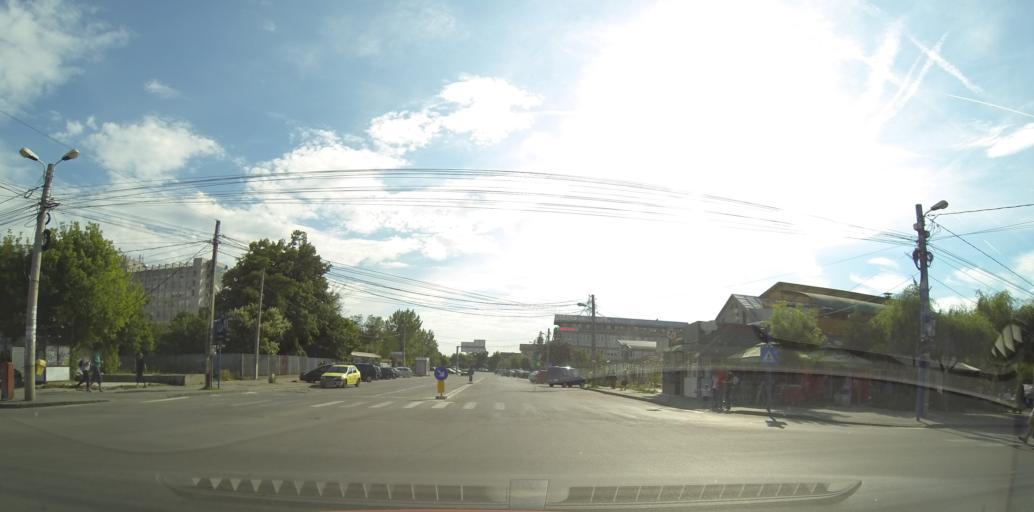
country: RO
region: Dolj
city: Craiova
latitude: 44.3072
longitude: 23.7933
